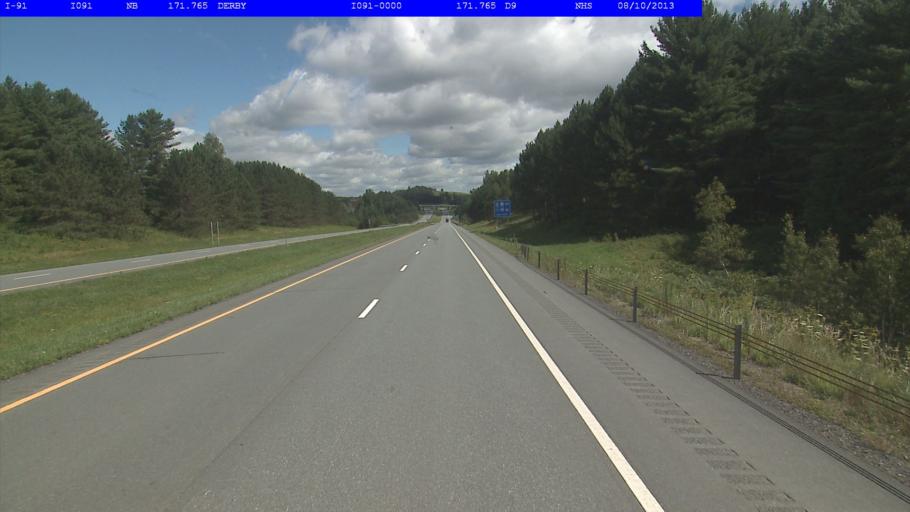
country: US
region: Vermont
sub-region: Orleans County
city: Newport
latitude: 44.9442
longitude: -72.1566
